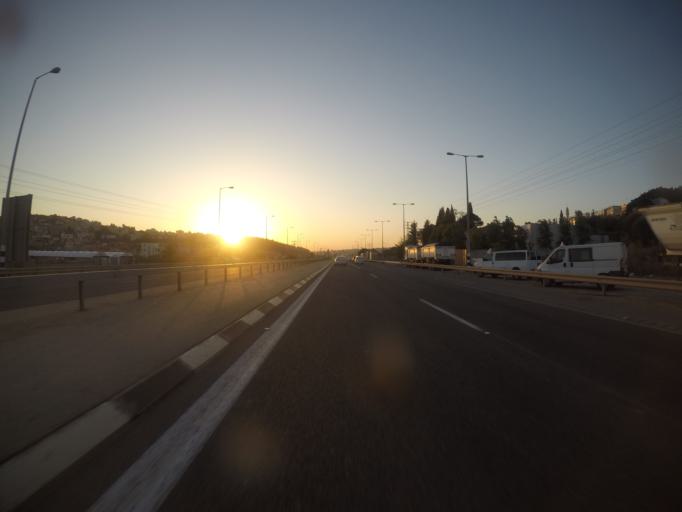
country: PS
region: West Bank
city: Barta`ah ash Sharqiyah
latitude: 32.5023
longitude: 35.0819
